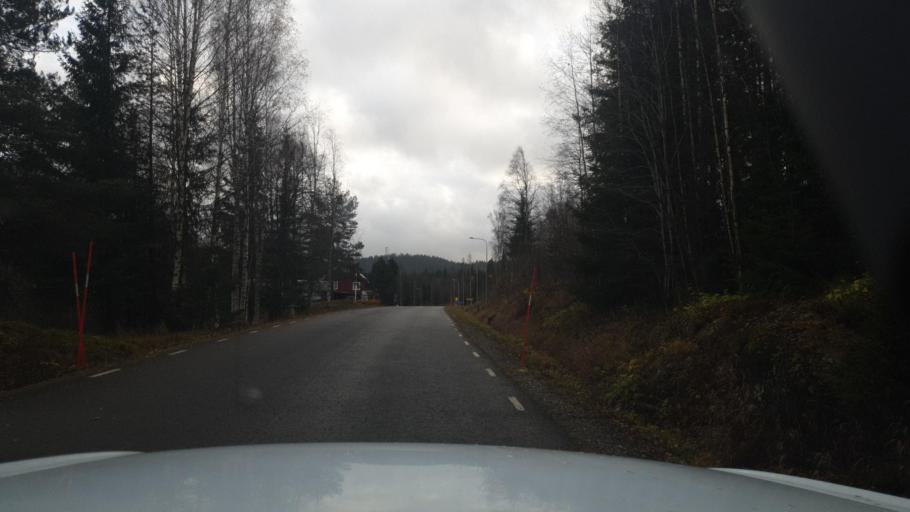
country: SE
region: Vaermland
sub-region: Eda Kommun
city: Charlottenberg
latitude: 60.0222
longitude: 12.6192
